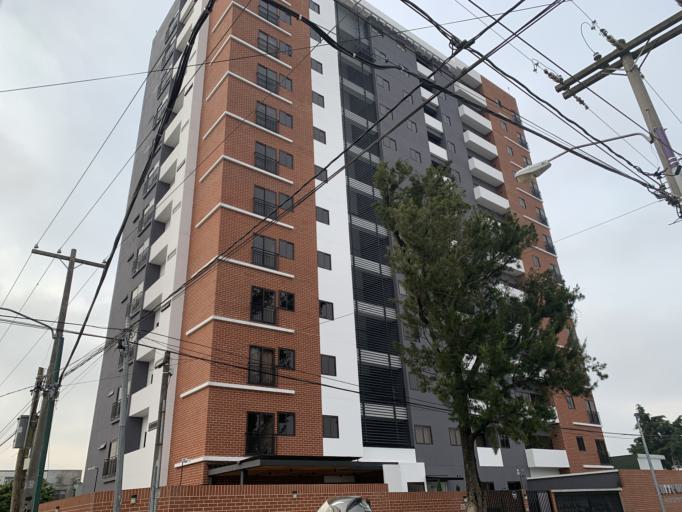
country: GT
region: Guatemala
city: Guatemala City
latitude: 14.6030
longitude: -90.5503
